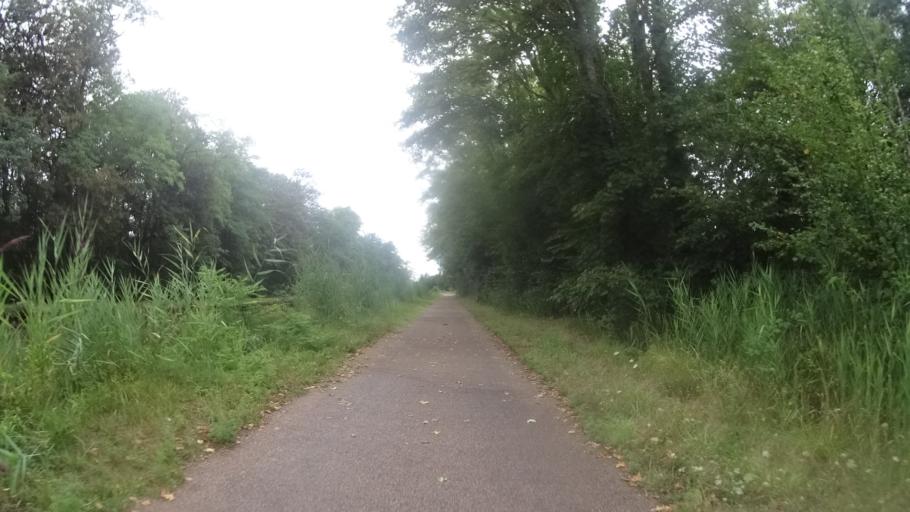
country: FR
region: Bourgogne
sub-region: Departement de la Nievre
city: Saint-Leger-des-Vignes
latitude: 46.8204
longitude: 3.4128
